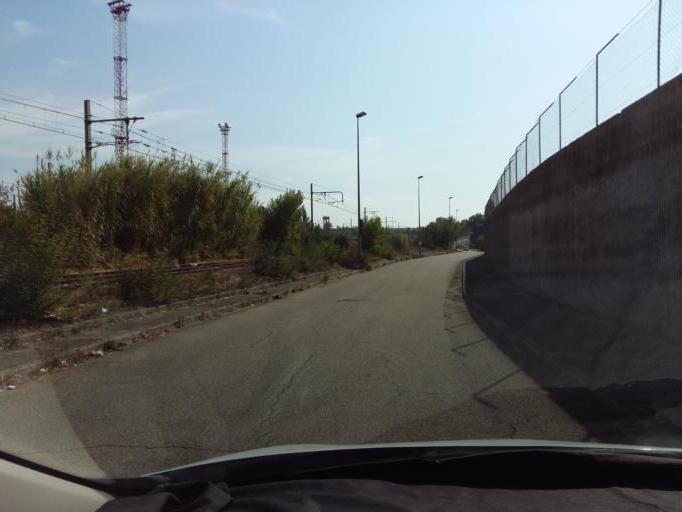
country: FR
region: Provence-Alpes-Cote d'Azur
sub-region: Departement du Vaucluse
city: Avignon
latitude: 43.9290
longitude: 4.7939
